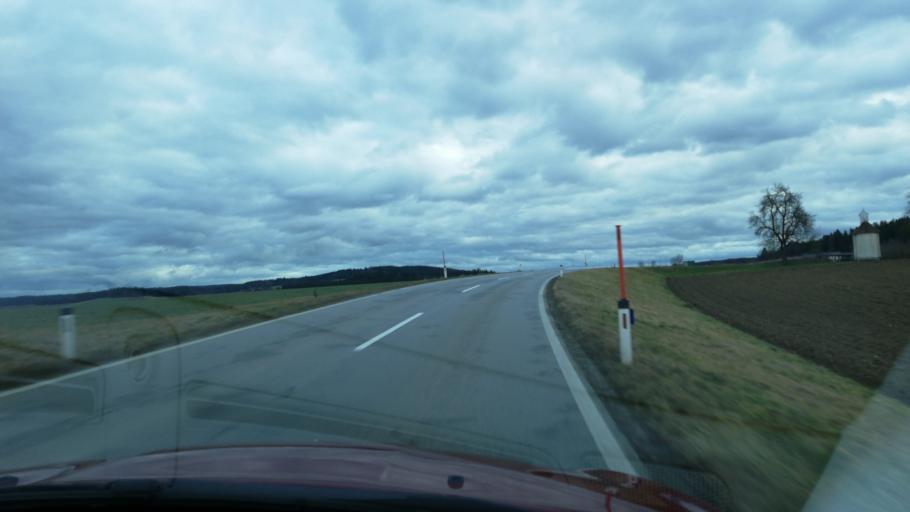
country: AT
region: Upper Austria
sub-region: Politischer Bezirk Braunau am Inn
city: Altheim
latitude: 48.2684
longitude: 13.3121
